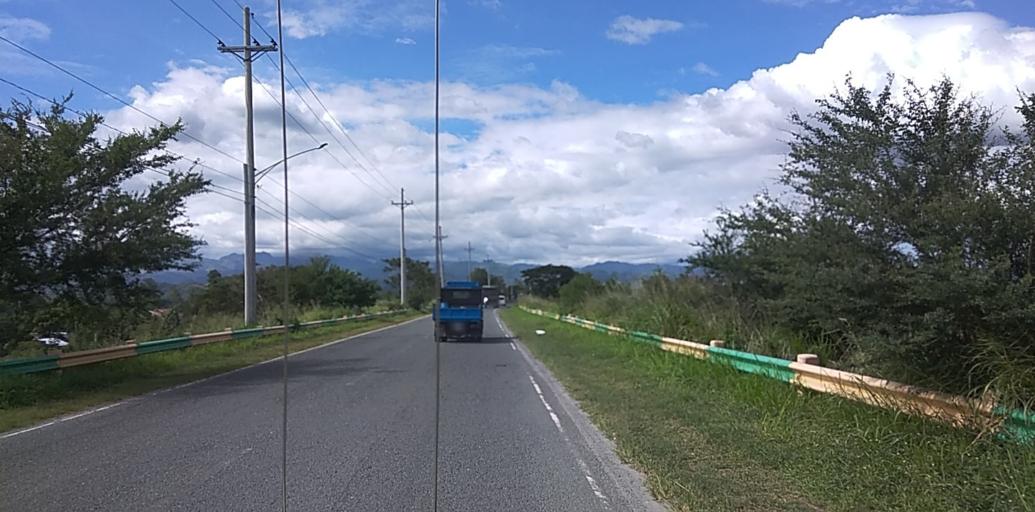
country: PH
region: Central Luzon
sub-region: Province of Pampanga
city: Porac
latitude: 15.0849
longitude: 120.5434
